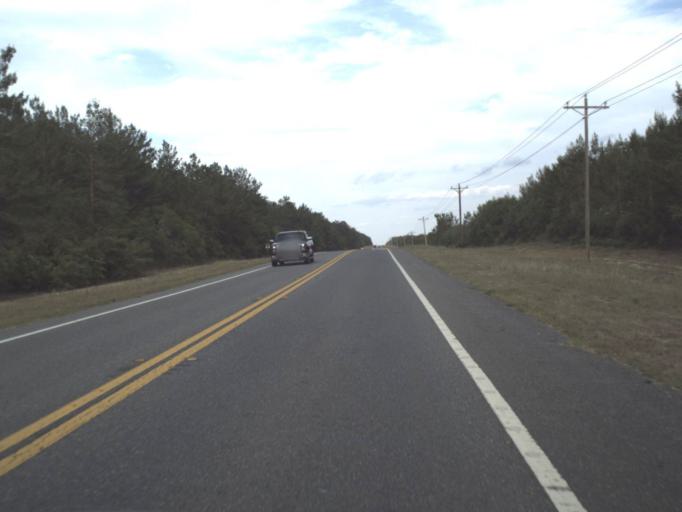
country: US
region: Florida
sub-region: Lake County
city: Astor
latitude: 29.1775
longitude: -81.7558
